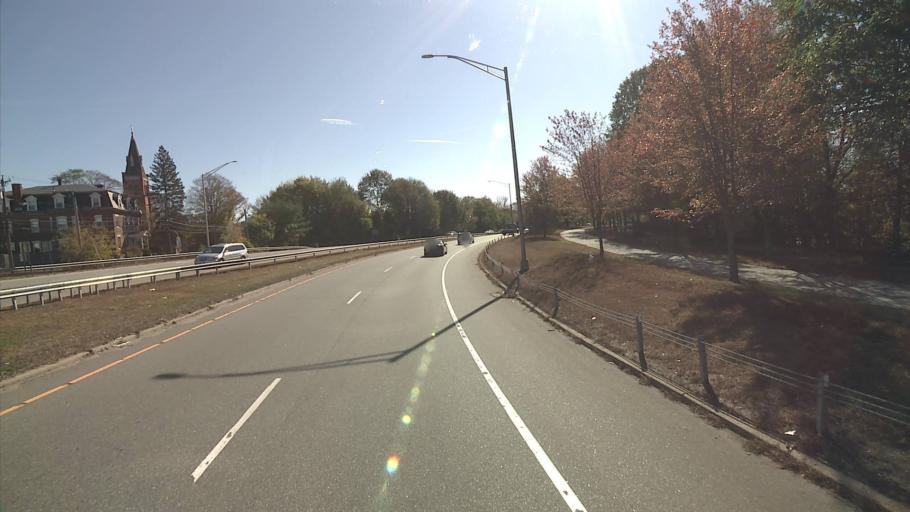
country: US
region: Connecticut
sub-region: Windham County
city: Danielson
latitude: 41.8014
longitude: -71.8862
